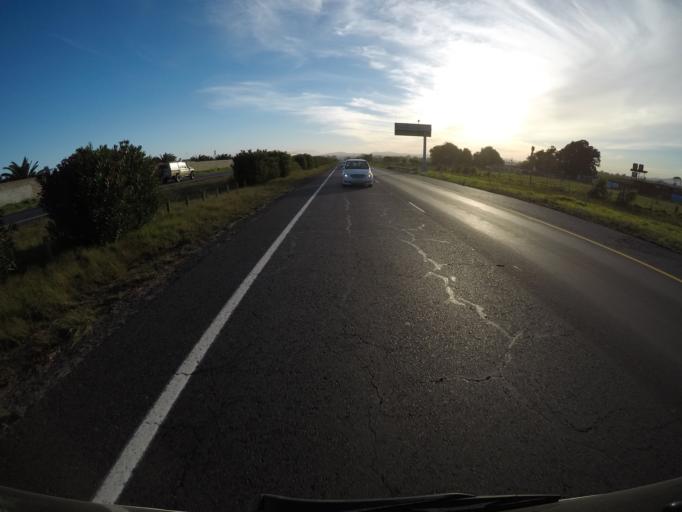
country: ZA
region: Western Cape
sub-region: City of Cape Town
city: Kraaifontein
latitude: -33.8302
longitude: 18.7543
